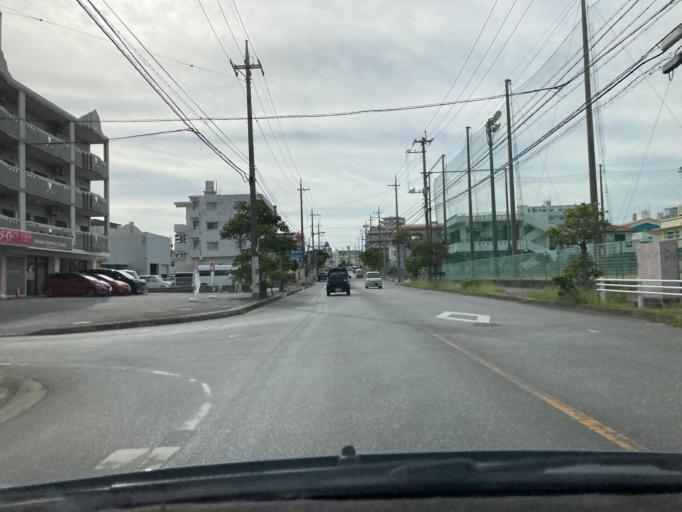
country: JP
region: Okinawa
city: Okinawa
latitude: 26.3433
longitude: 127.8256
